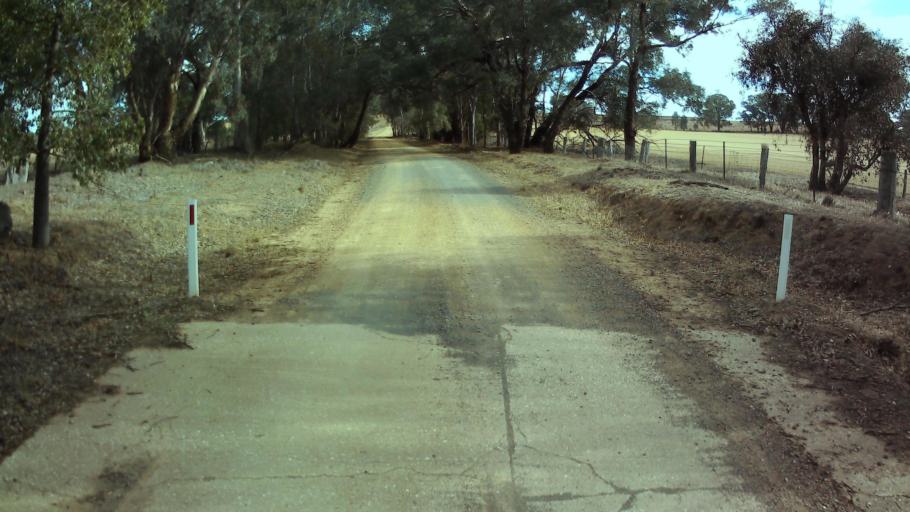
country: AU
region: New South Wales
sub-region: Weddin
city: Grenfell
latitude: -33.8998
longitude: 148.2033
